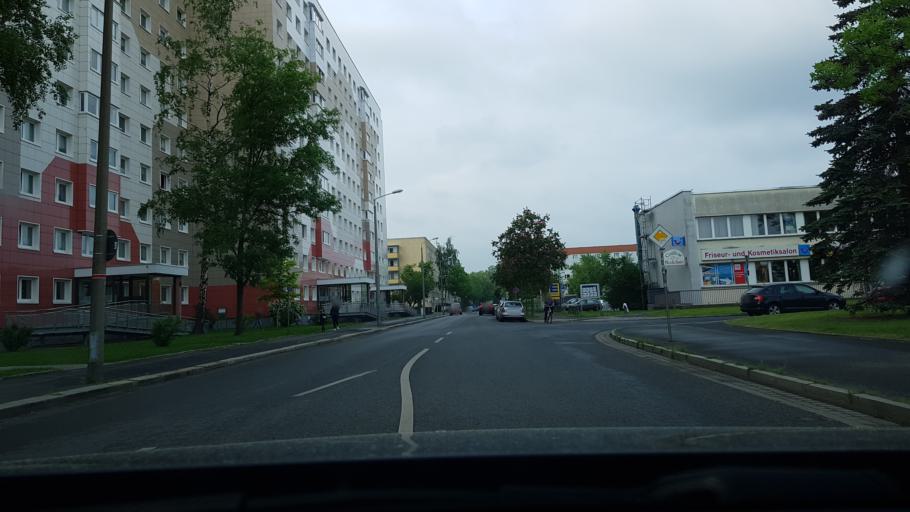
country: DE
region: Saxony
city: Heidenau
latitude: 51.0123
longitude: 13.8234
